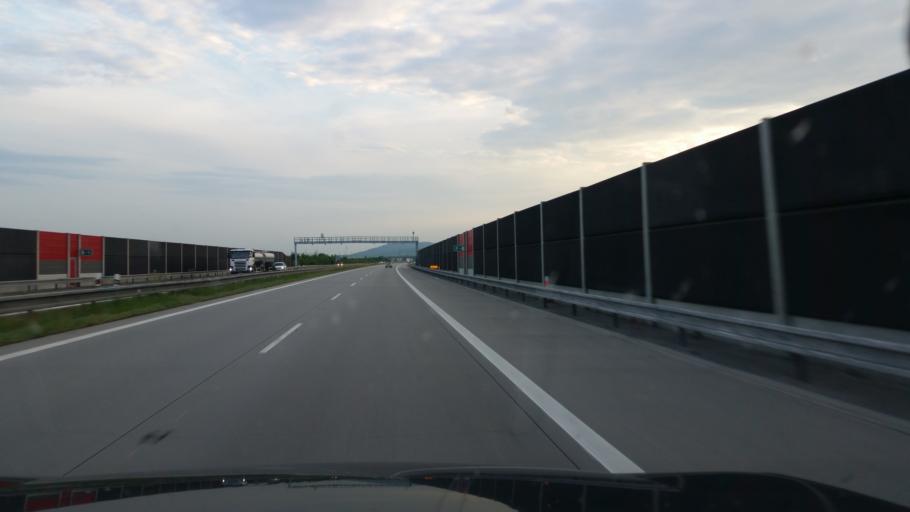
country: CZ
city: Kunin
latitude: 49.6979
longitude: 17.9764
